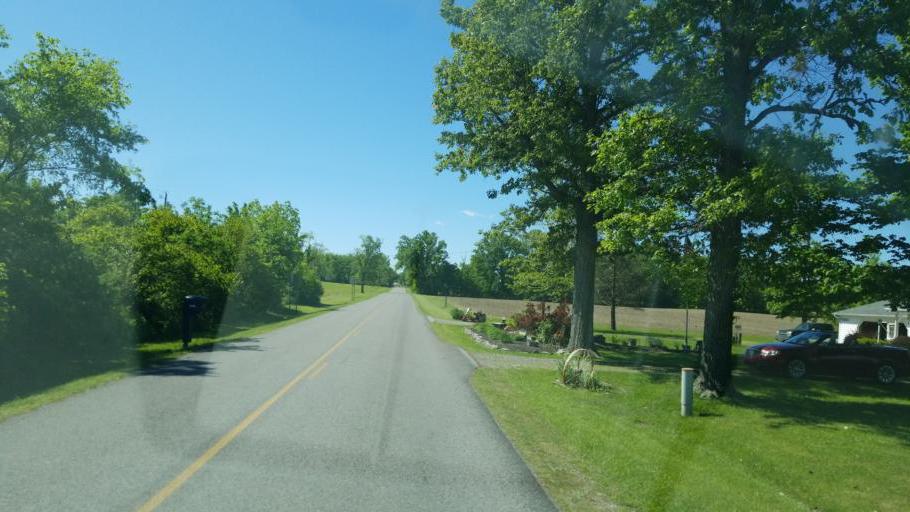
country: US
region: Ohio
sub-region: Logan County
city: Northwood
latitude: 40.4546
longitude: -83.7201
